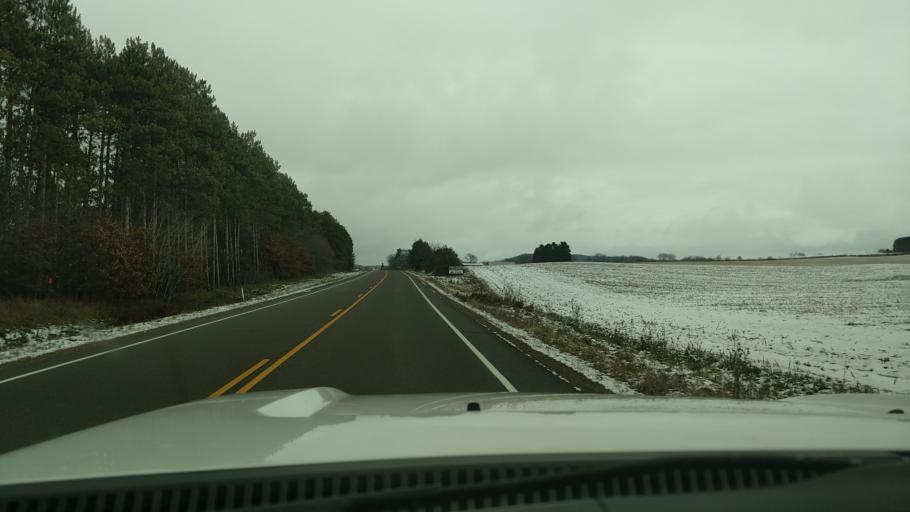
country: US
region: Wisconsin
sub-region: Dunn County
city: Colfax
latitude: 45.1426
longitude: -91.6706
